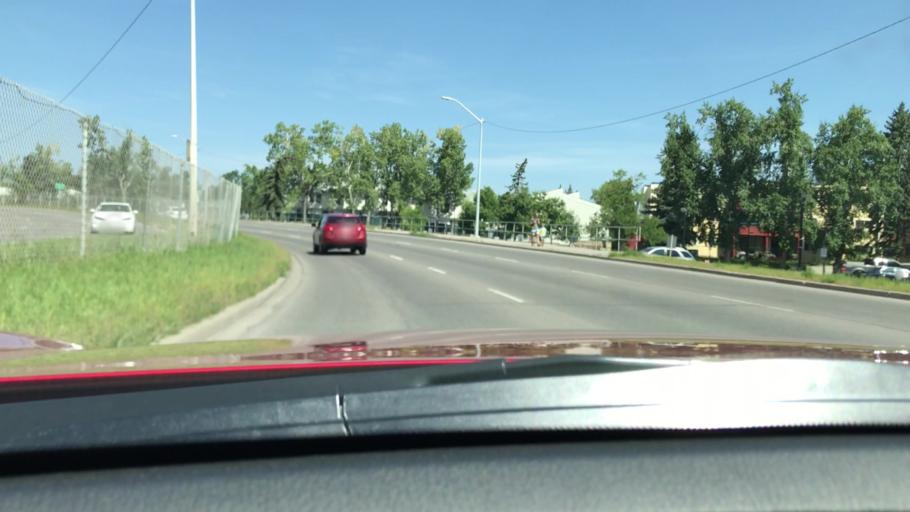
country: CA
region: Alberta
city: Calgary
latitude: 51.0436
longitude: -114.1383
